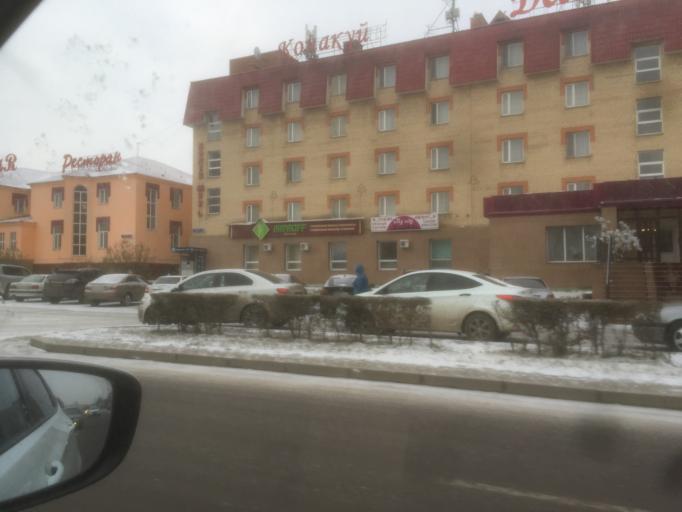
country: KZ
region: Astana Qalasy
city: Astana
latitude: 51.1503
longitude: 71.4572
